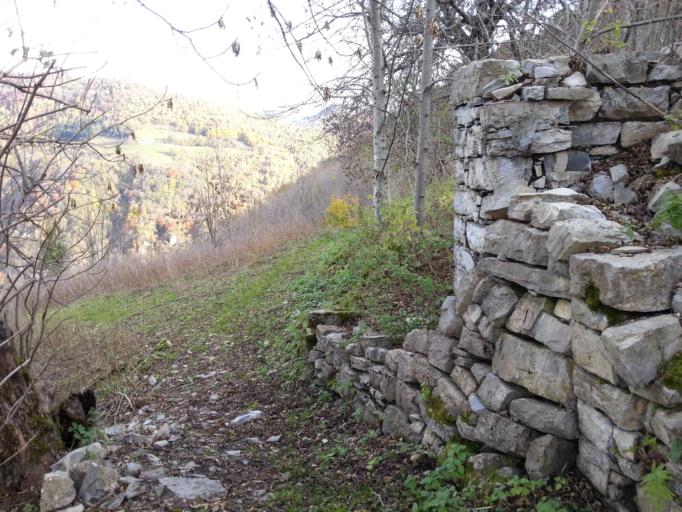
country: IT
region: Lombardy
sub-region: Provincia di Lecco
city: Morterone
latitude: 45.8776
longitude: 9.4971
